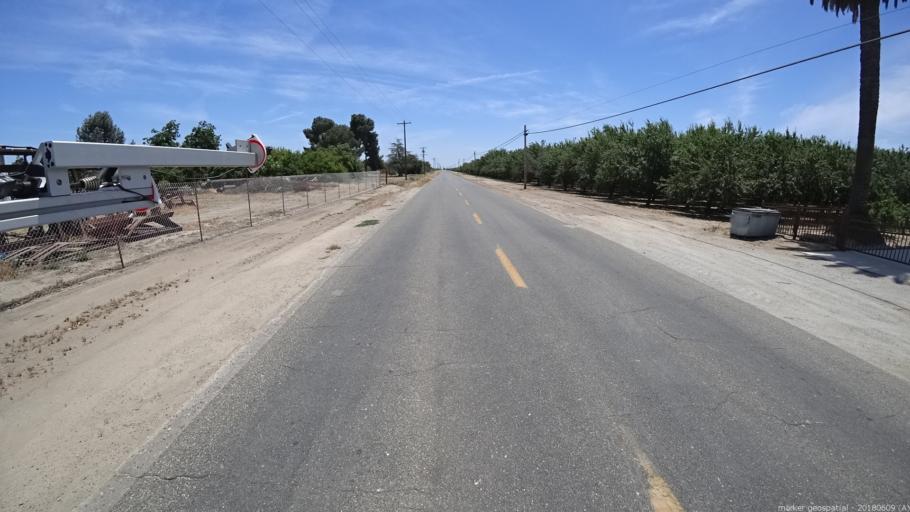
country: US
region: California
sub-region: Madera County
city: Parkwood
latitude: 36.9042
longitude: -120.0923
